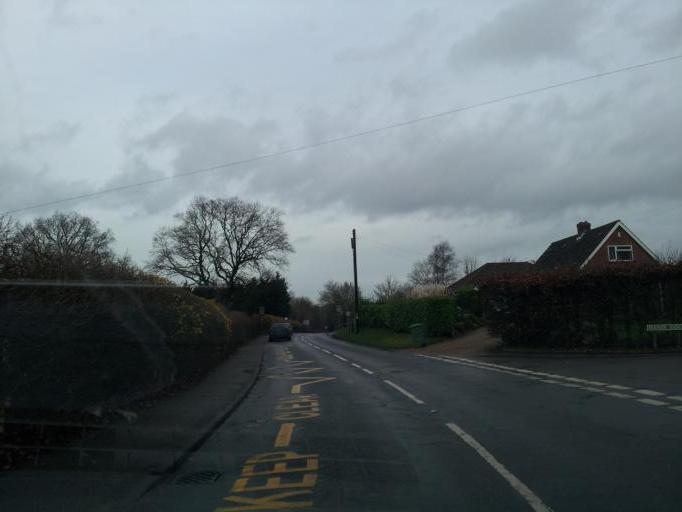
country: GB
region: England
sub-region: Norfolk
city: Brundall
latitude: 52.6369
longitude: 1.4488
